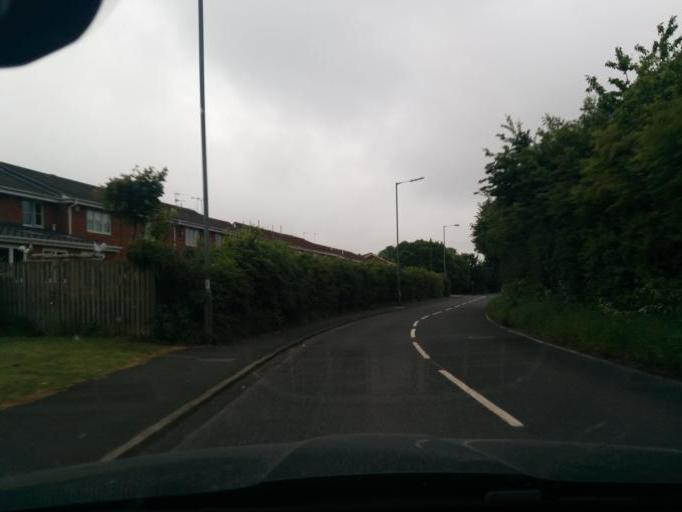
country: GB
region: England
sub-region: Northumberland
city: Cramlington
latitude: 55.1014
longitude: -1.5692
